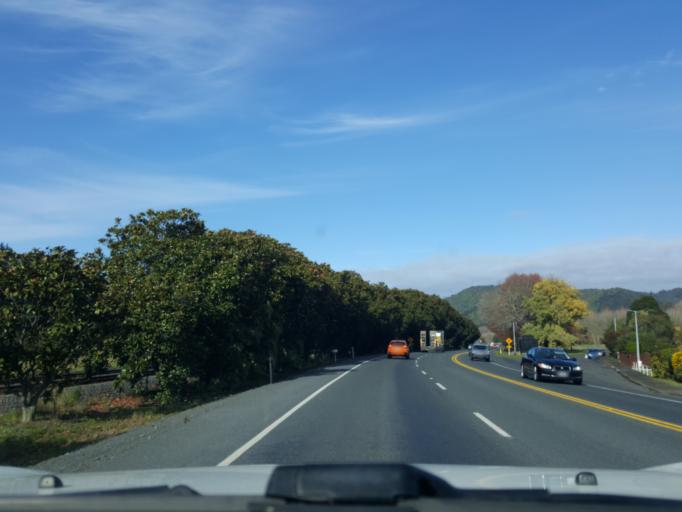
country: NZ
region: Waikato
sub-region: Waikato District
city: Ngaruawahia
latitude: -37.5829
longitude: 175.1595
